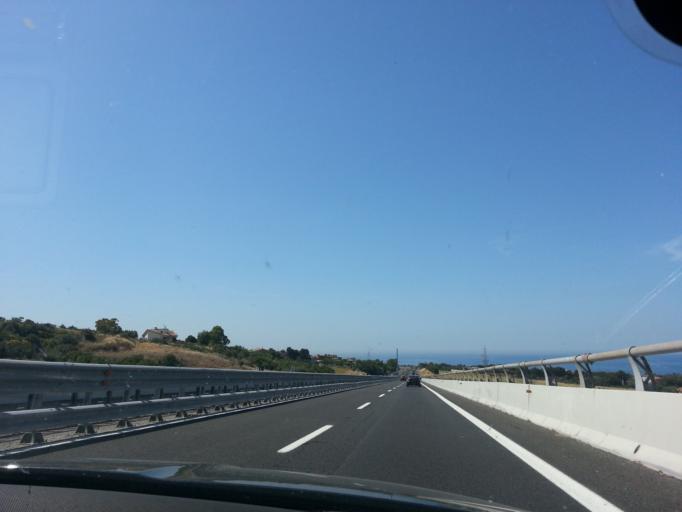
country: IT
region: Latium
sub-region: Citta metropolitana di Roma Capitale
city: Civitavecchia
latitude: 42.0846
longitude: 11.8271
